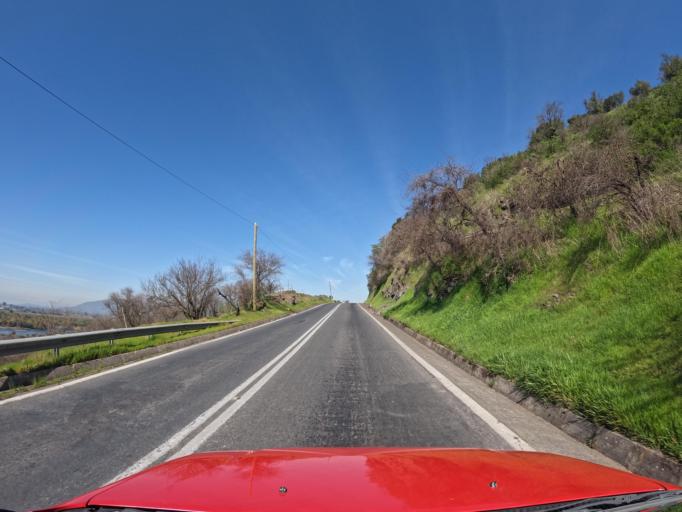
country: CL
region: Maule
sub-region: Provincia de Curico
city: Rauco
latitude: -34.9746
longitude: -71.3825
